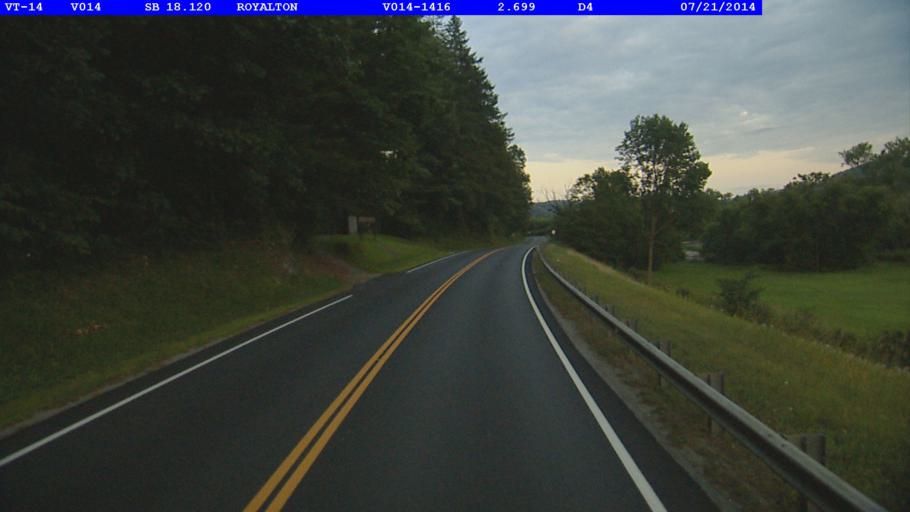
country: US
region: Vermont
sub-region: Orange County
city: Randolph
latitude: 43.8259
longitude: -72.5251
